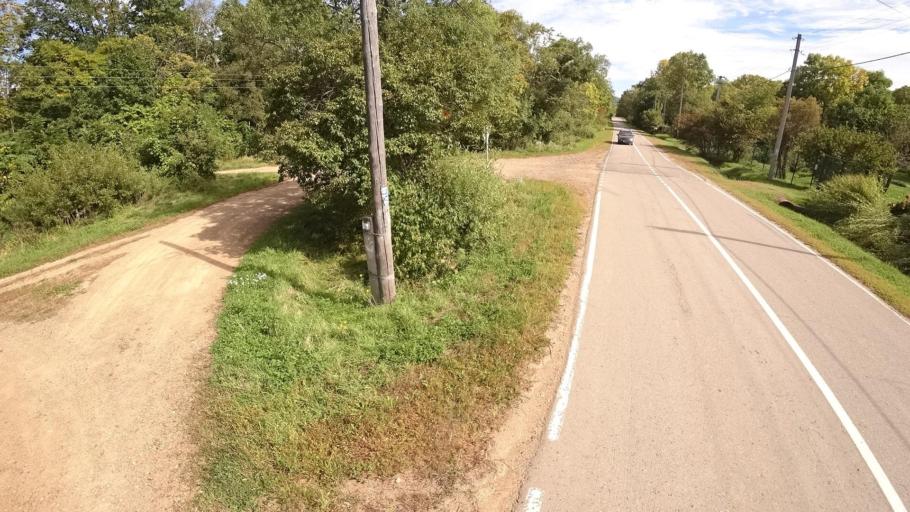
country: RU
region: Primorskiy
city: Yakovlevka
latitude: 44.3963
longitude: 133.6029
